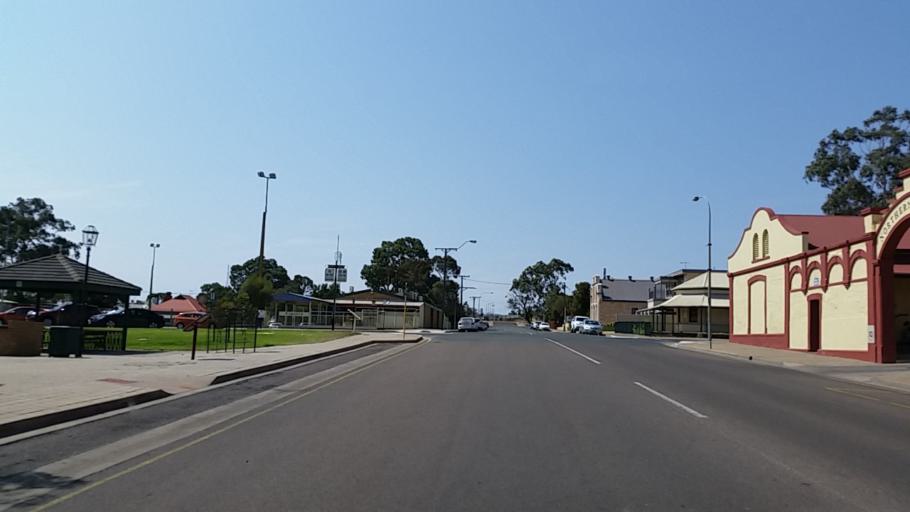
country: AU
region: South Australia
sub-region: Port Augusta
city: Port Augusta West
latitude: -32.4921
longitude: 137.7639
